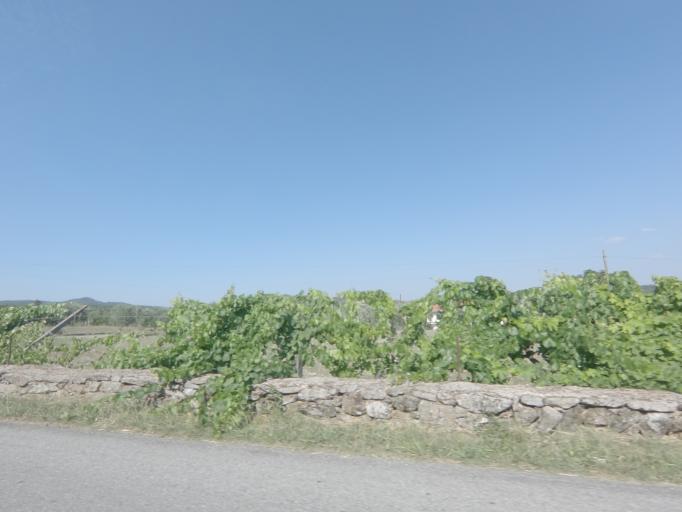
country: PT
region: Viseu
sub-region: Moimenta da Beira
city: Moimenta da Beira
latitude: 40.9721
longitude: -7.5912
